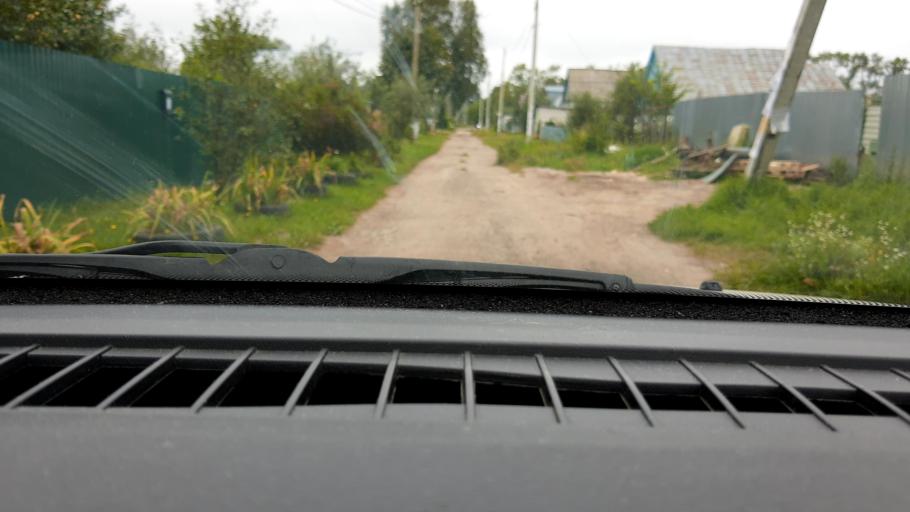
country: RU
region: Nizjnij Novgorod
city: Gorbatovka
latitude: 56.2677
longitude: 43.7520
